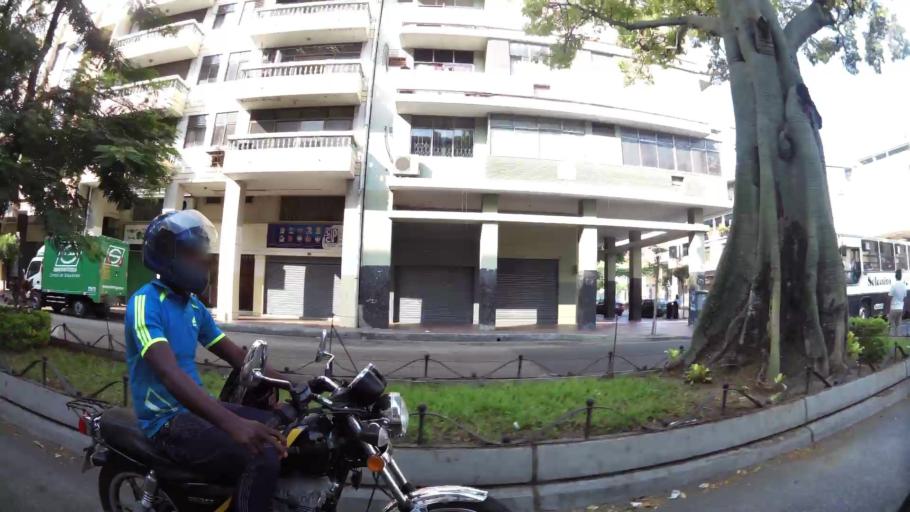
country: EC
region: Guayas
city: Guayaquil
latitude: -2.1969
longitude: -79.8830
